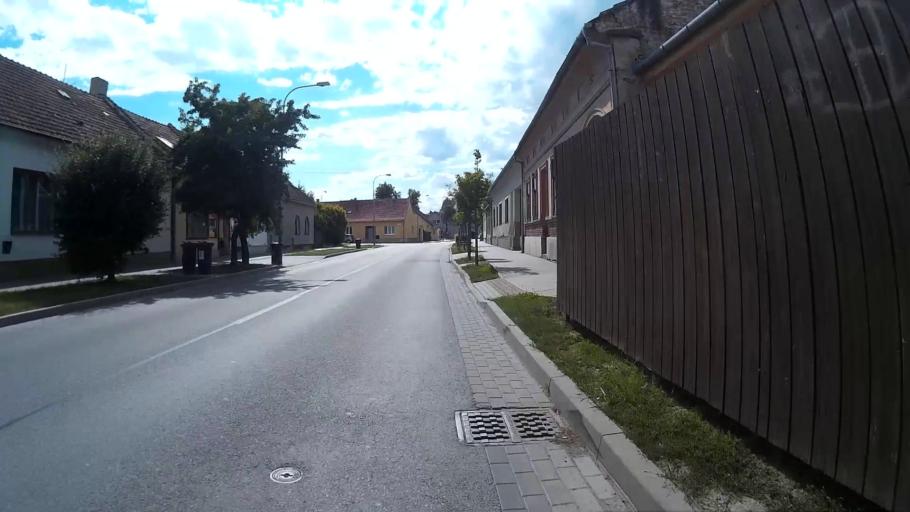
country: CZ
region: South Moravian
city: Ostopovice
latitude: 49.1647
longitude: 16.5631
